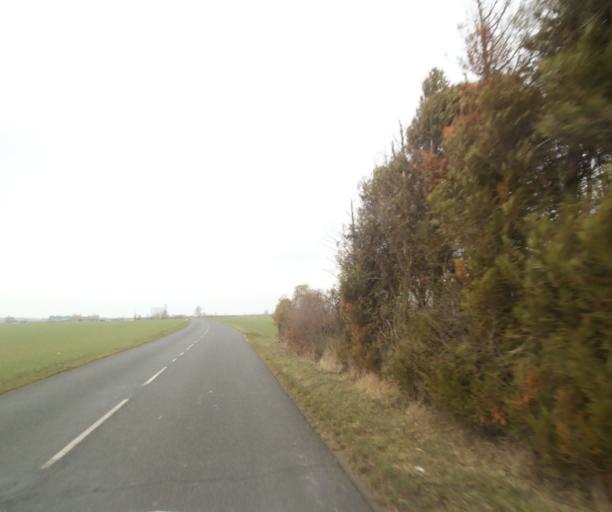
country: FR
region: Champagne-Ardenne
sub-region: Departement de la Haute-Marne
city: Villiers-en-Lieu
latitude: 48.6541
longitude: 4.7838
